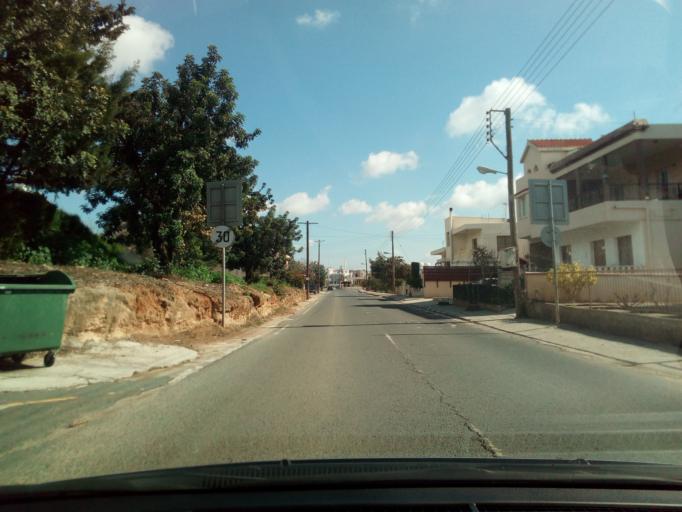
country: CY
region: Pafos
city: Mesogi
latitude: 34.8178
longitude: 32.4496
